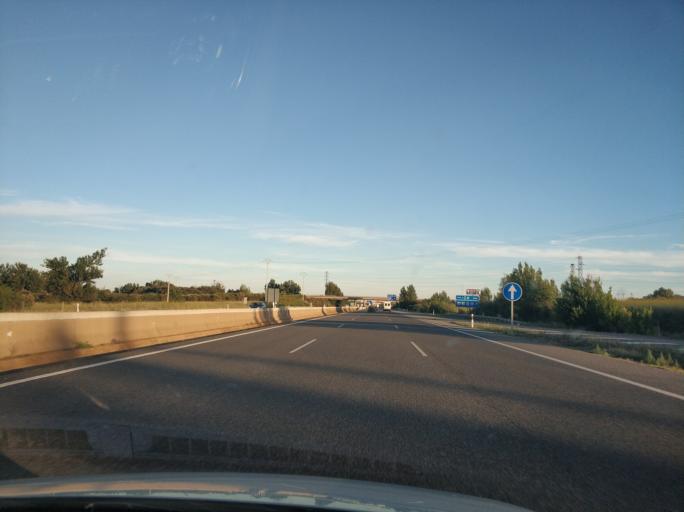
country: ES
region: Castille and Leon
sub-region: Provincia de Zamora
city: Benavente
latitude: 42.0115
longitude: -5.6638
